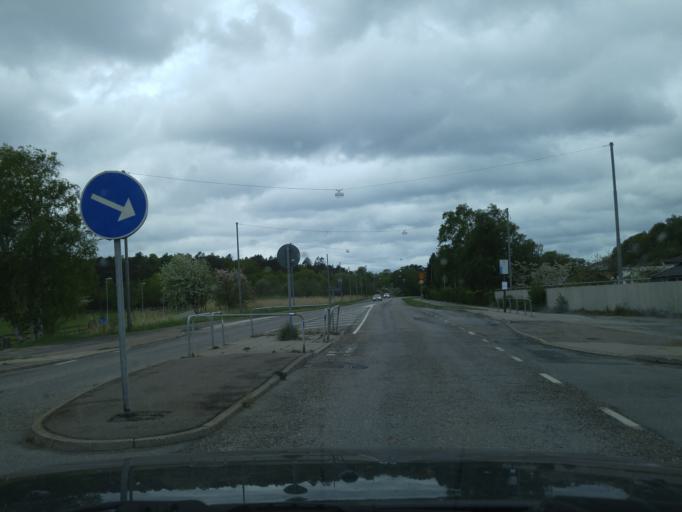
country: SE
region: Vaestra Goetaland
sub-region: Goteborg
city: Majorna
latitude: 57.6368
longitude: 11.9085
